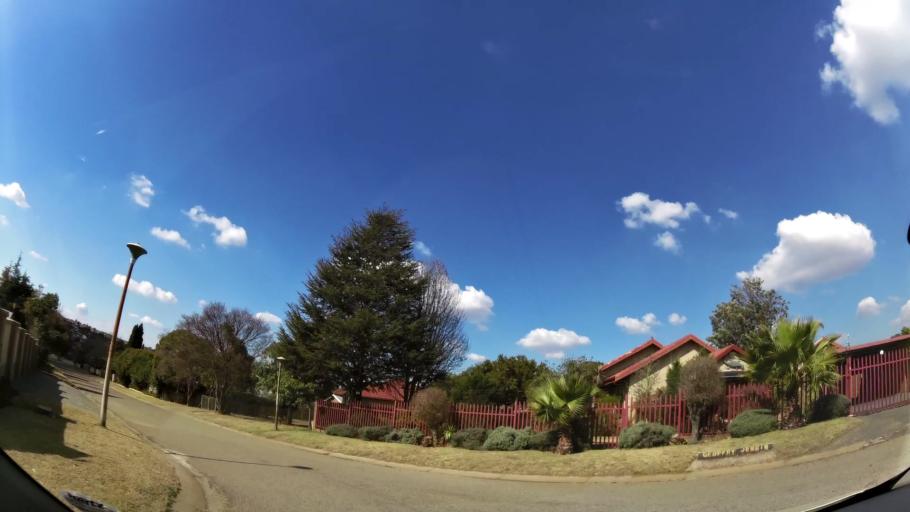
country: ZA
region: Mpumalanga
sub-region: Nkangala District Municipality
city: Witbank
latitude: -25.9362
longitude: 29.2409
